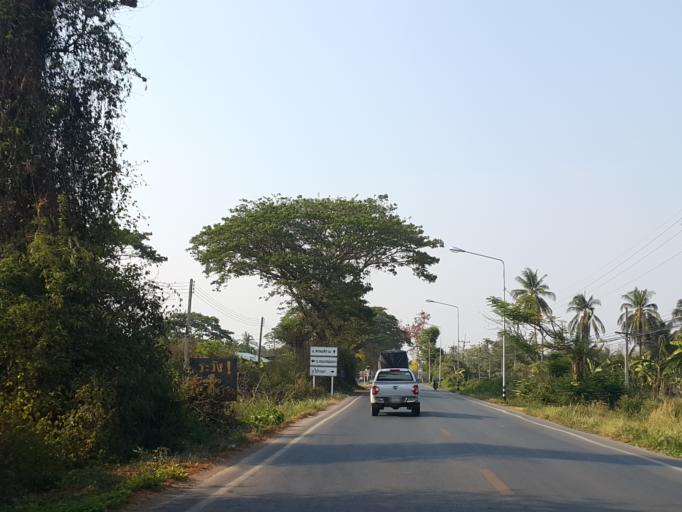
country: TH
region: Phitsanulok
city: Phrom Phiram
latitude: 16.9797
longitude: 100.2118
